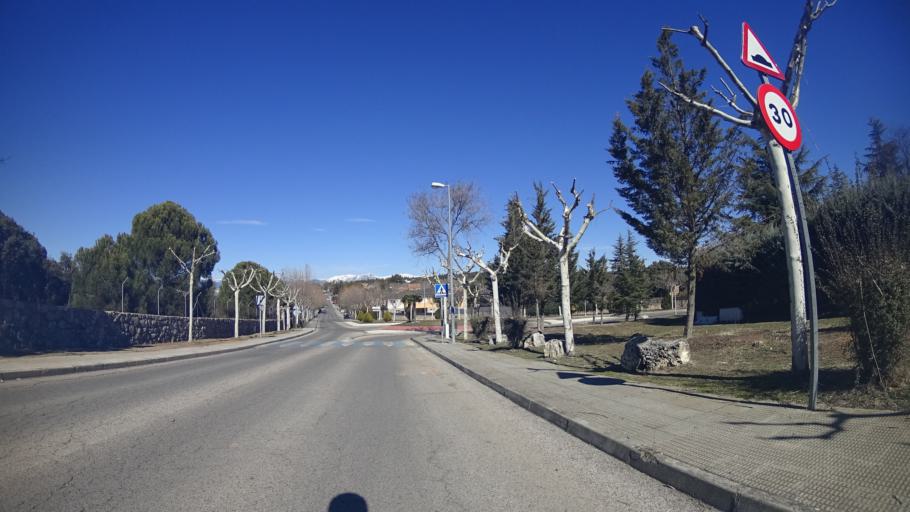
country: ES
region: Madrid
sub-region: Provincia de Madrid
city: Colmenarejo
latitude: 40.5529
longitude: -4.0133
